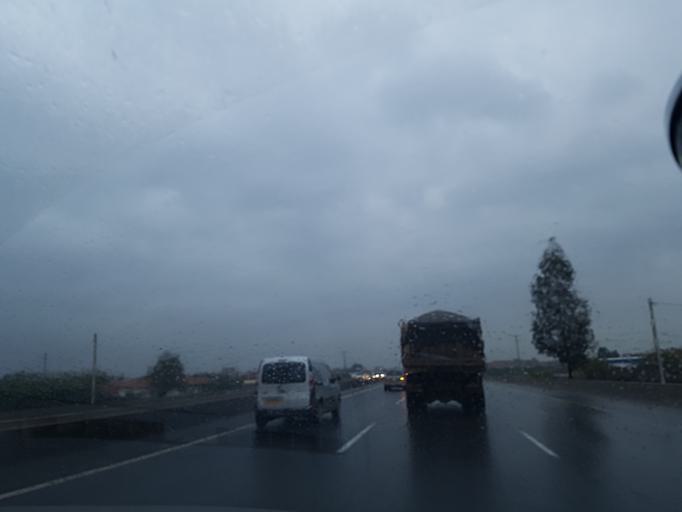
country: DZ
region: Blida
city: Meftah
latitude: 36.6587
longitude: 3.2563
